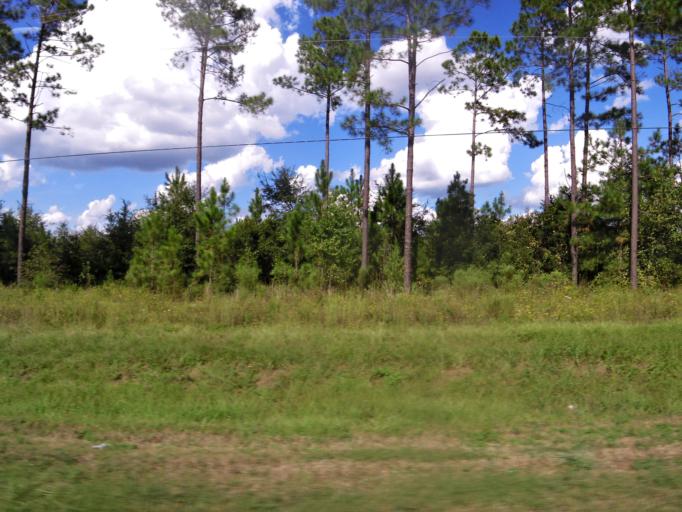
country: US
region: Georgia
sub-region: Lowndes County
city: Valdosta
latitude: 30.8029
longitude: -83.2019
